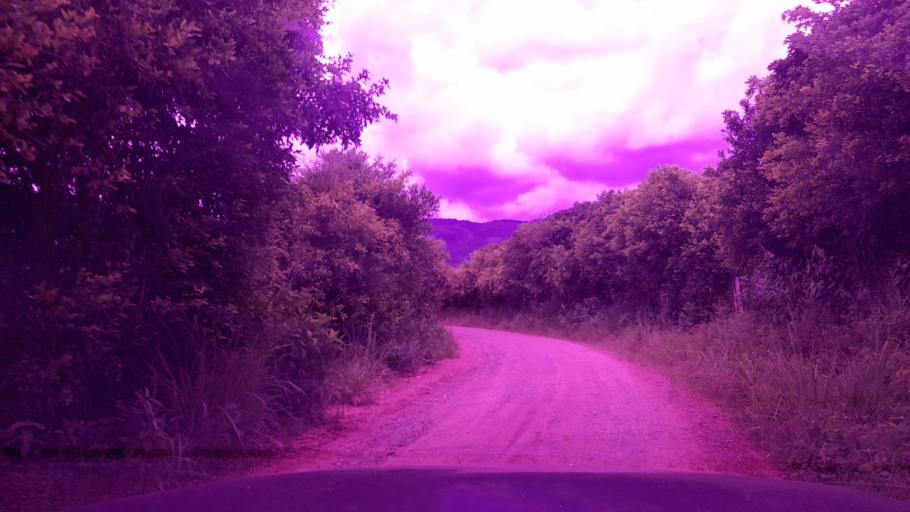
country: CO
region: Valle del Cauca
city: Andalucia
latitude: 4.1691
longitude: -76.0853
